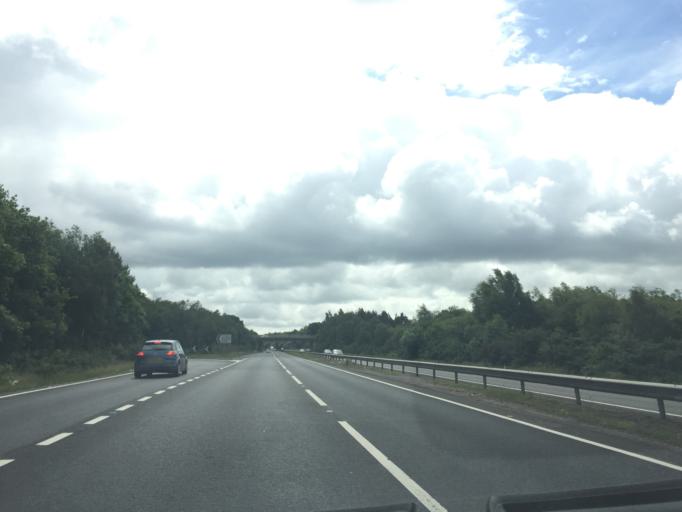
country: GB
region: England
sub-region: Dorset
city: Ferndown
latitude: 50.8174
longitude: -1.8914
